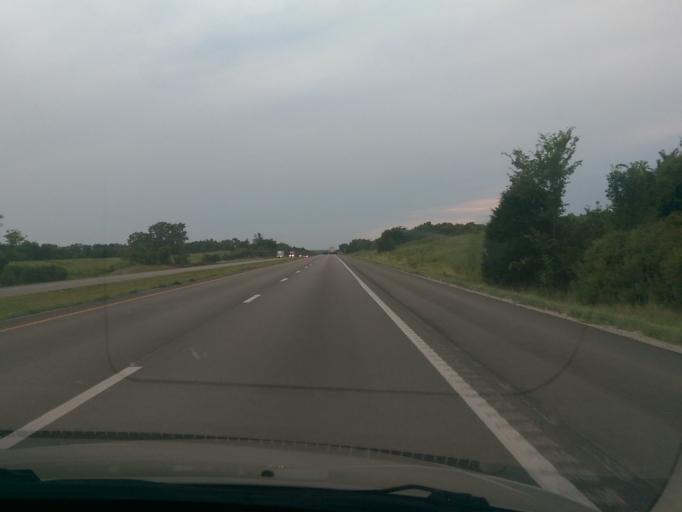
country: US
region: Missouri
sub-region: Andrew County
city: Savannah
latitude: 39.9497
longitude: -94.9485
